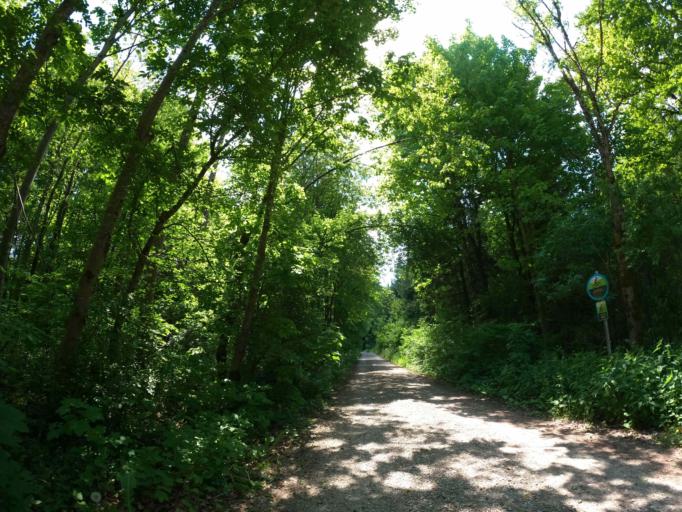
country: DE
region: Bavaria
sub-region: Upper Bavaria
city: Oberhaching
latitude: 48.0213
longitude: 11.6230
